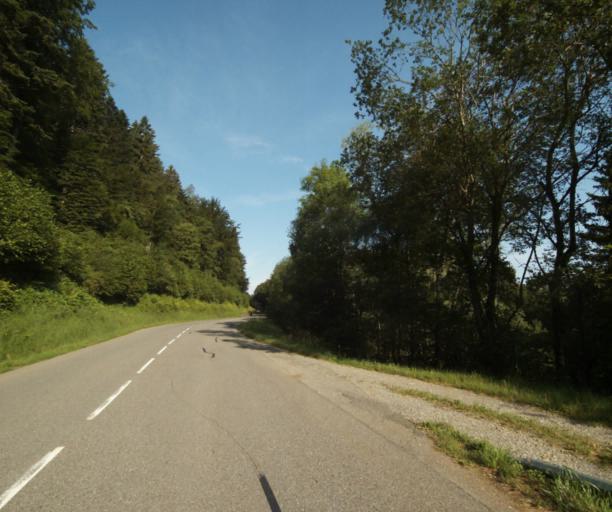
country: FR
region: Rhone-Alpes
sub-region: Departement de la Haute-Savoie
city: Lyaud
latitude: 46.3401
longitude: 6.5452
